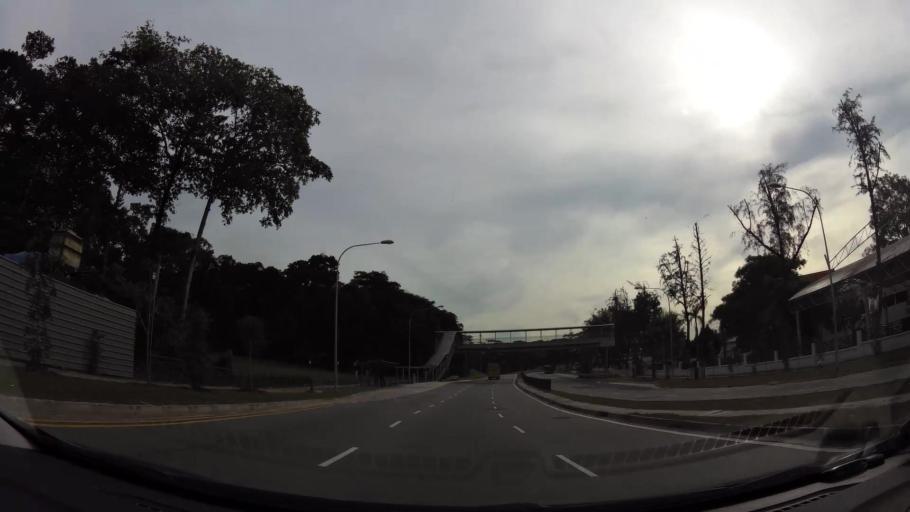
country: MY
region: Johor
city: Johor Bahru
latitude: 1.3666
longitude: 103.6939
